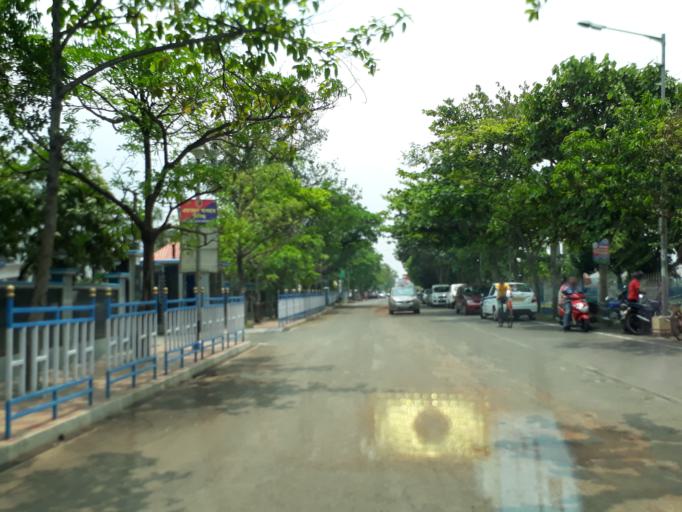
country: IN
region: West Bengal
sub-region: Purba Medinipur
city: Haldia
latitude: 22.0604
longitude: 88.0773
